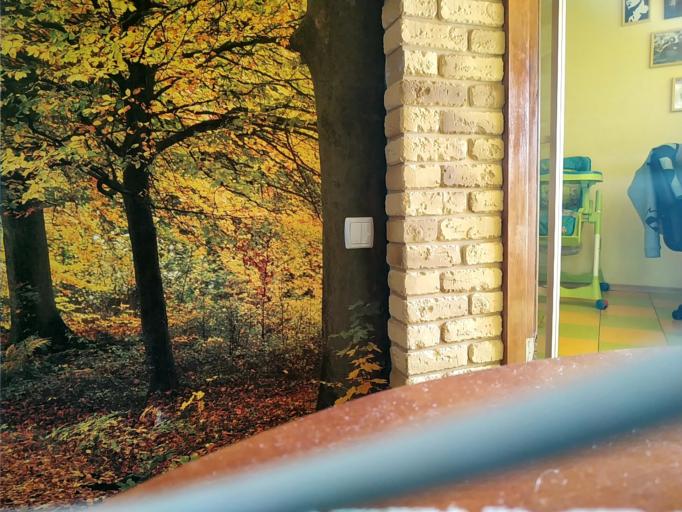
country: RU
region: Tverskaya
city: Rameshki
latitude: 57.3079
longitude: 35.9091
